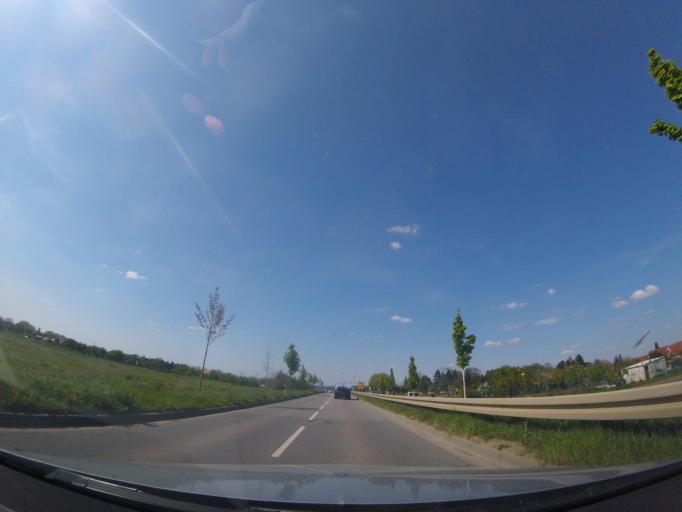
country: DE
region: Hesse
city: Griesheim
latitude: 49.8554
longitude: 8.5483
